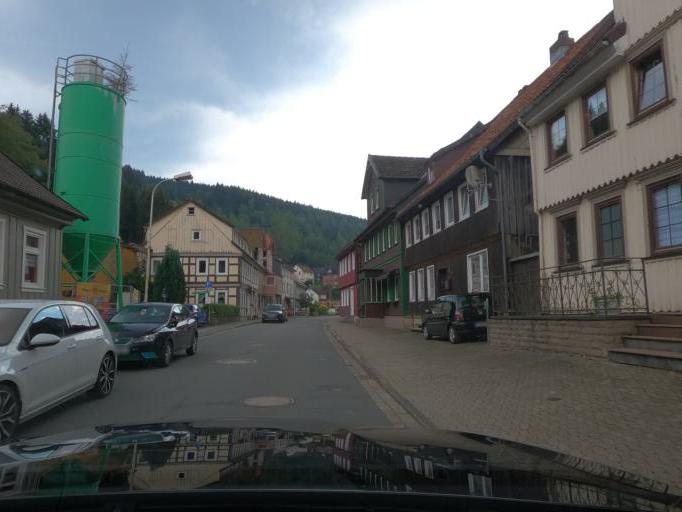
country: DE
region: Lower Saxony
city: Wildemann
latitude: 51.8258
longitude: 10.2837
